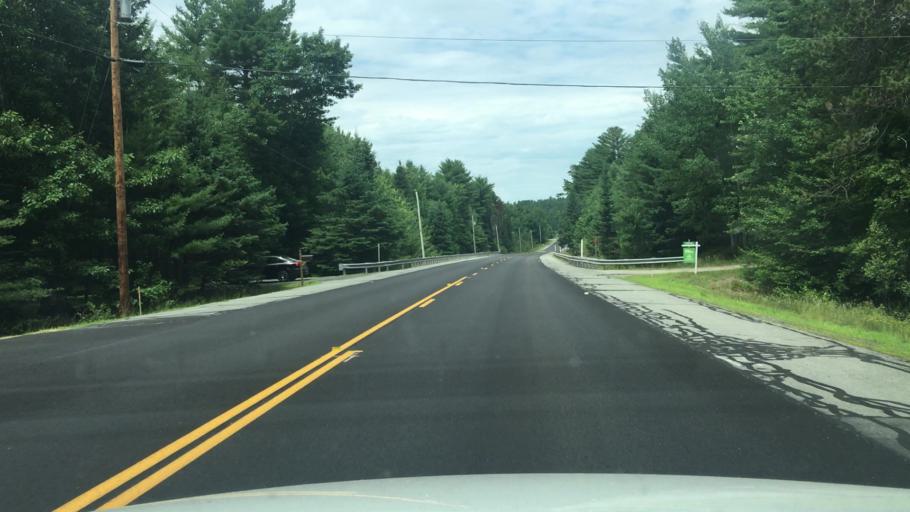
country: US
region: Maine
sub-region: Waldo County
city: Palermo
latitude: 44.4006
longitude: -69.4765
